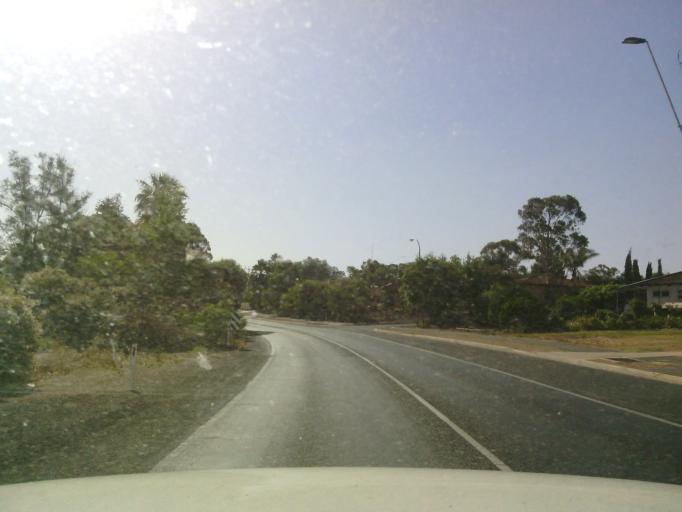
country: AU
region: South Australia
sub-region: Berri and Barmera
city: Berri
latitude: -34.2825
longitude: 140.5923
